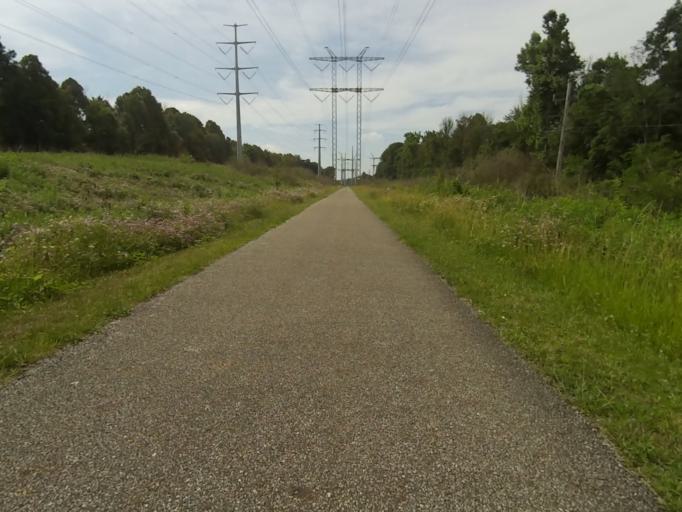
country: US
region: Ohio
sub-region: Cuyahoga County
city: Walton Hills
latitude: 41.3348
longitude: -81.5706
